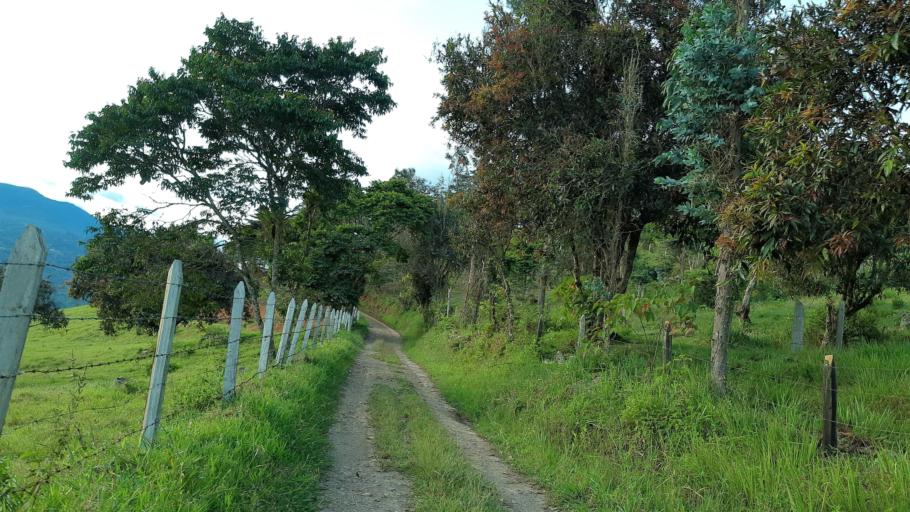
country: CO
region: Boyaca
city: Garagoa
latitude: 5.0562
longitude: -73.3777
